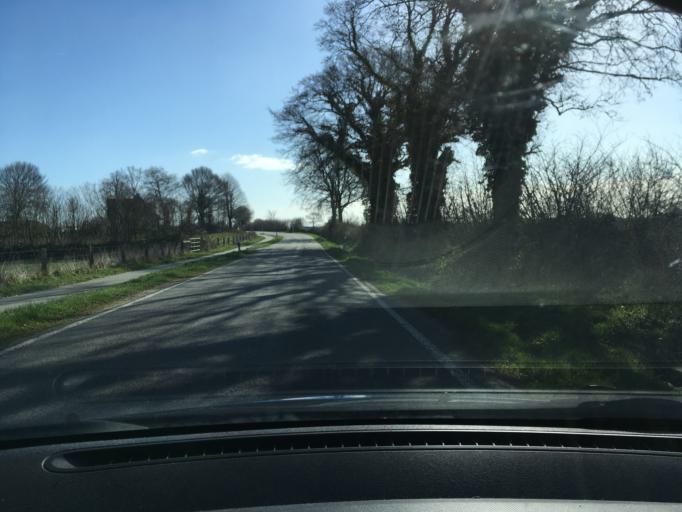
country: DE
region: Schleswig-Holstein
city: Fahrdorf
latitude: 54.5050
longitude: 9.6173
